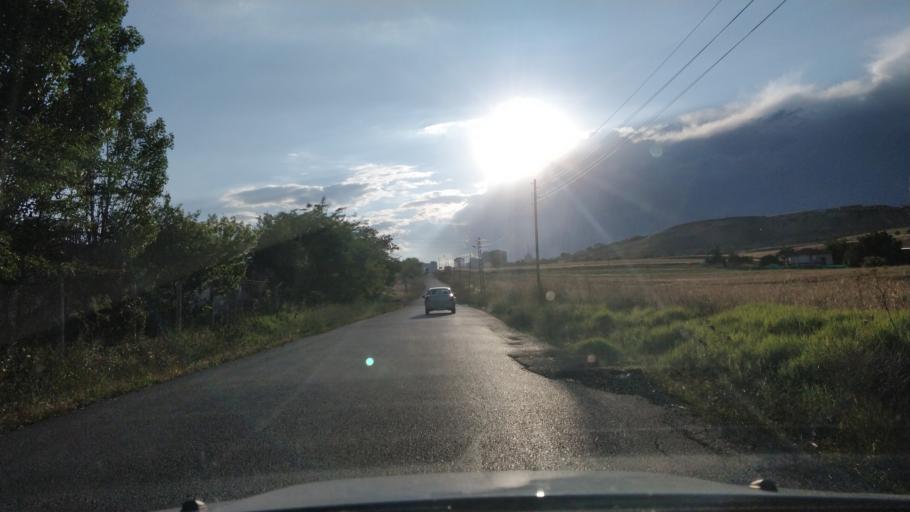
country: TR
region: Ankara
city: Etimesgut
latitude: 39.8262
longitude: 32.5668
